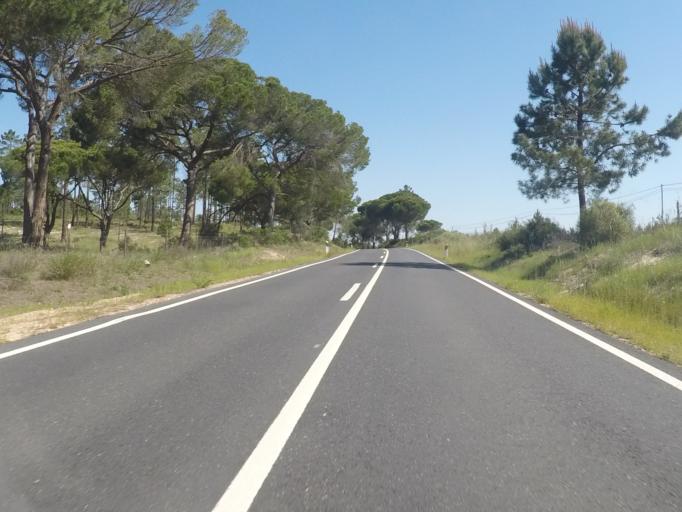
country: PT
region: Setubal
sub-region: Grandola
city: Grandola
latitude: 38.2779
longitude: -8.7259
